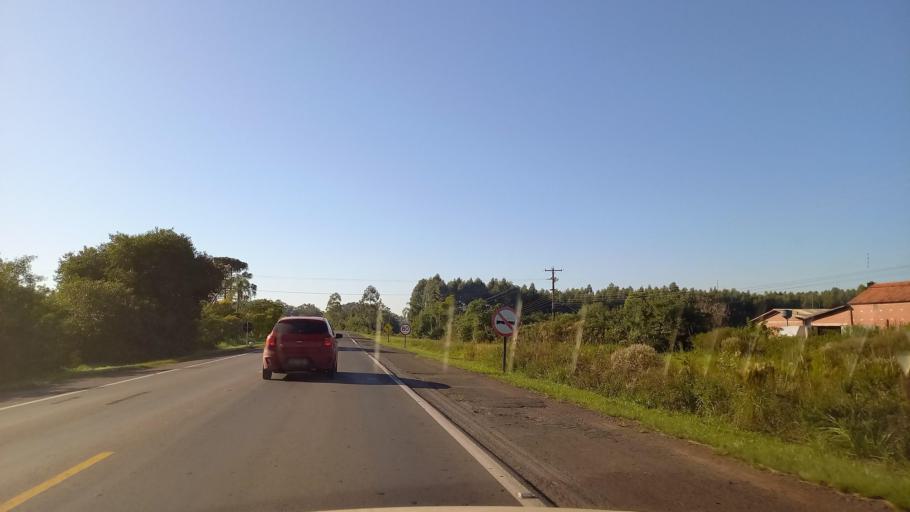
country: BR
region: Rio Grande do Sul
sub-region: Venancio Aires
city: Venancio Aires
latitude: -29.6686
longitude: -52.0409
